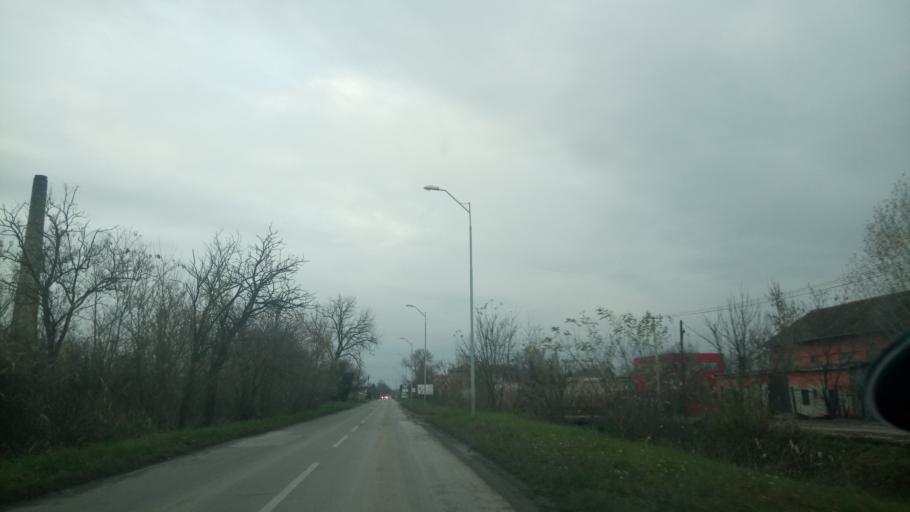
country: RS
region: Autonomna Pokrajina Vojvodina
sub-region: Sremski Okrug
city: Stara Pazova
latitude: 44.9719
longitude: 20.1634
